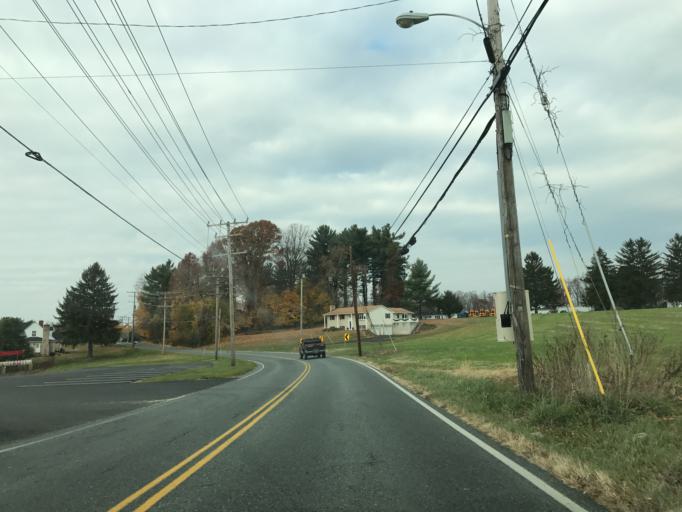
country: US
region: Maryland
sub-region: Harford County
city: Jarrettsville
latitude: 39.5902
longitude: -76.4311
